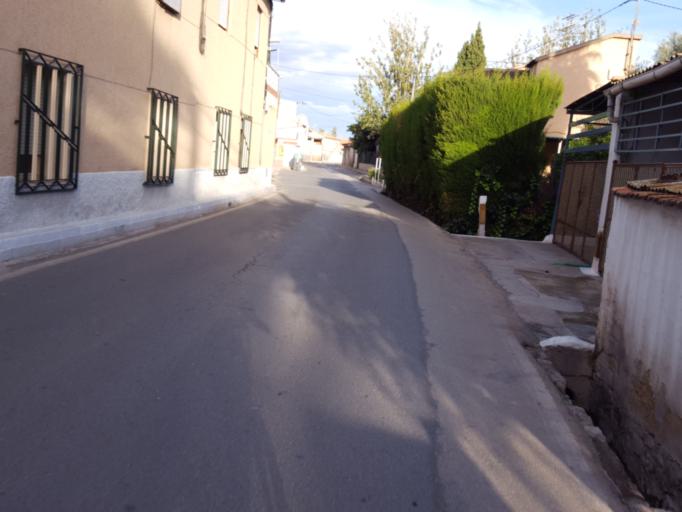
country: ES
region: Murcia
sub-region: Murcia
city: Murcia
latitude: 37.9879
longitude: -1.1603
